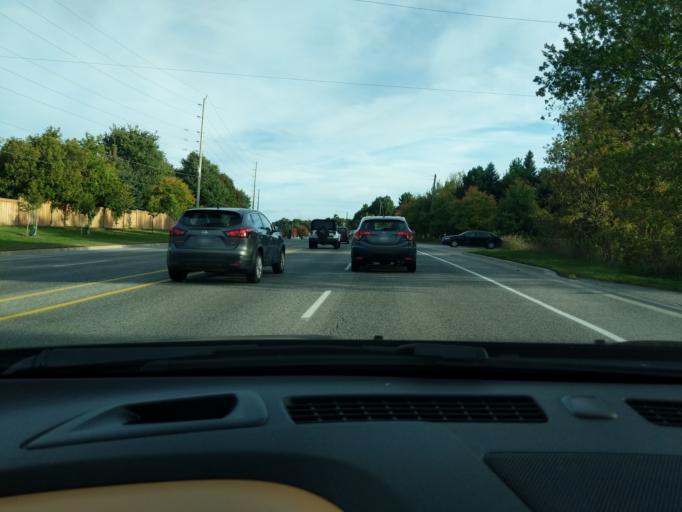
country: CA
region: Ontario
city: Newmarket
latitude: 44.0418
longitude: -79.5043
